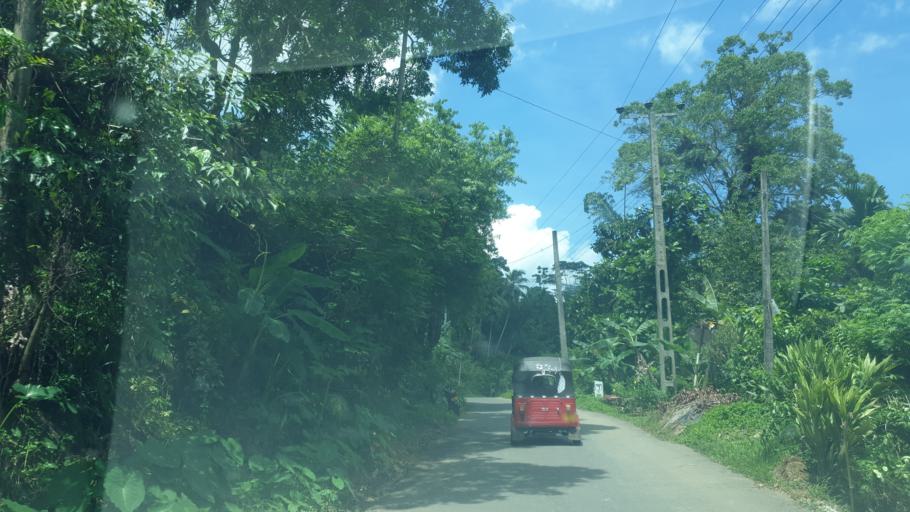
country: LK
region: Sabaragamuwa
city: Ratnapura
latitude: 6.4840
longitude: 80.4080
